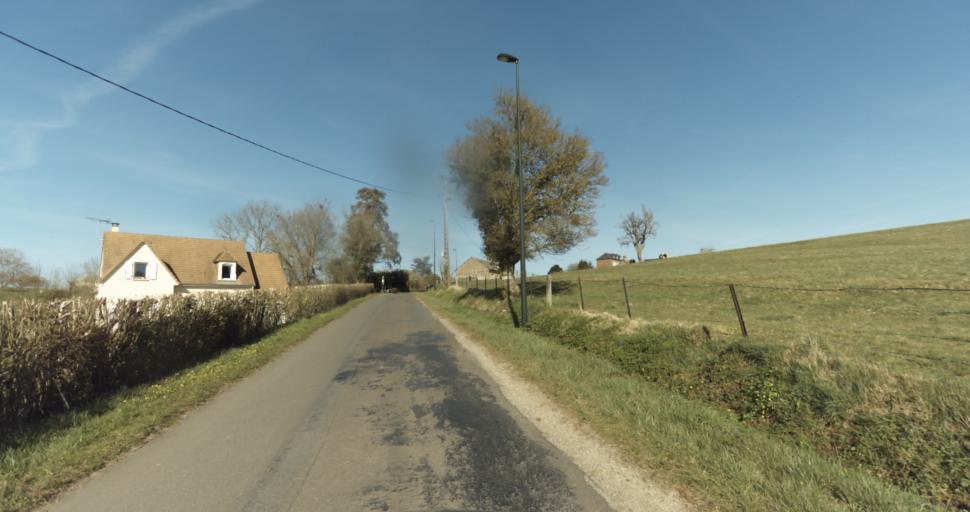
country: FR
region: Lower Normandy
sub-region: Departement du Calvados
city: Saint-Pierre-sur-Dives
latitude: 49.0218
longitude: 0.0511
